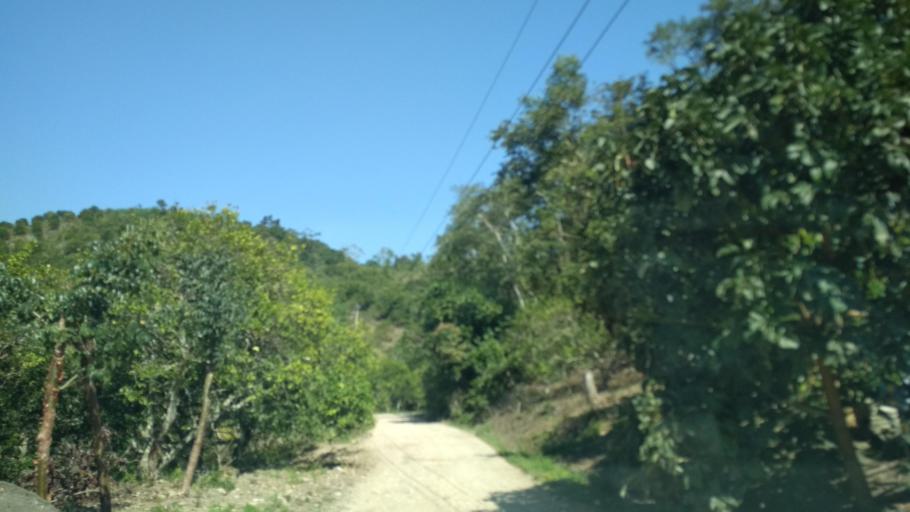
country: MX
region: Veracruz
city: Gutierrez Zamora
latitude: 20.4850
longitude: -97.1613
